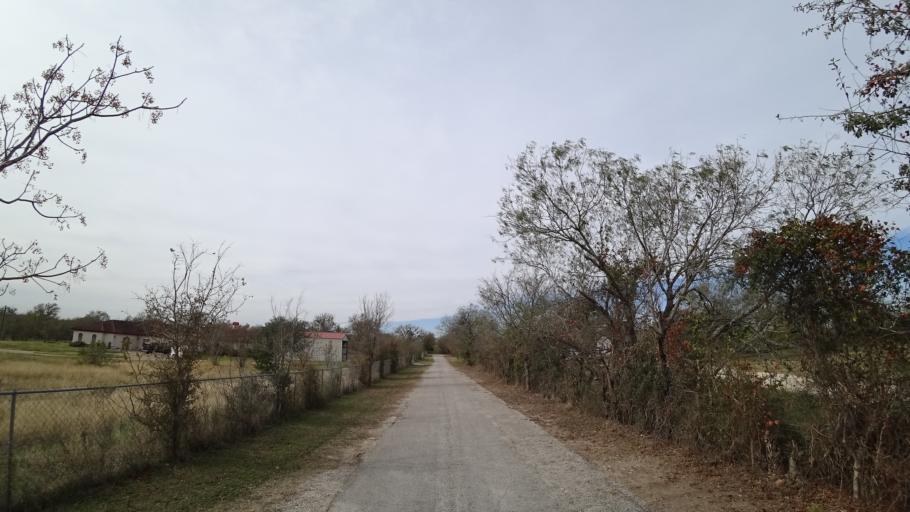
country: US
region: Texas
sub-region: Travis County
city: Garfield
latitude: 30.1457
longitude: -97.5797
